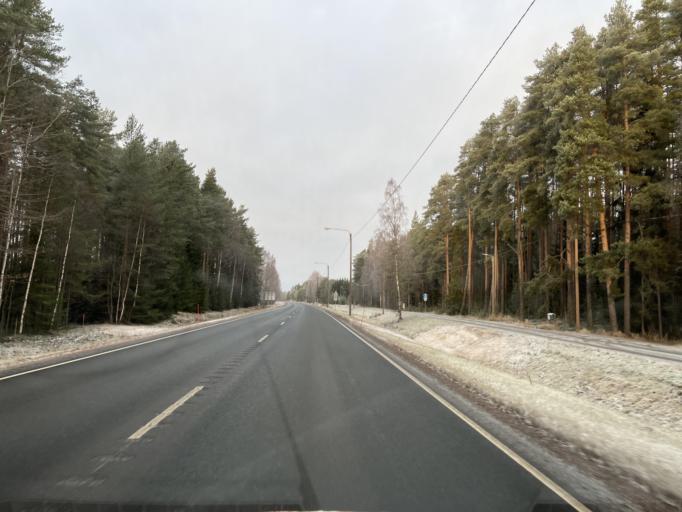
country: FI
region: Northern Ostrobothnia
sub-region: Oulu
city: Muhos
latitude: 64.8780
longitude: 25.8534
